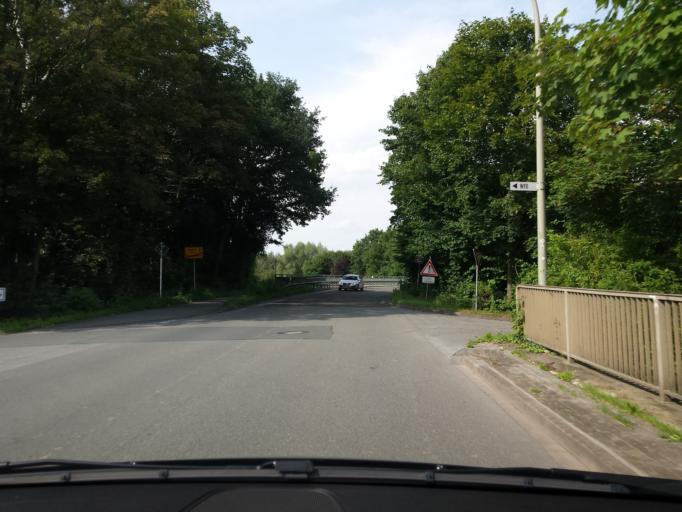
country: DE
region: North Rhine-Westphalia
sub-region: Regierungsbezirk Munster
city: Wadersloh
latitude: 51.6587
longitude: 8.2410
